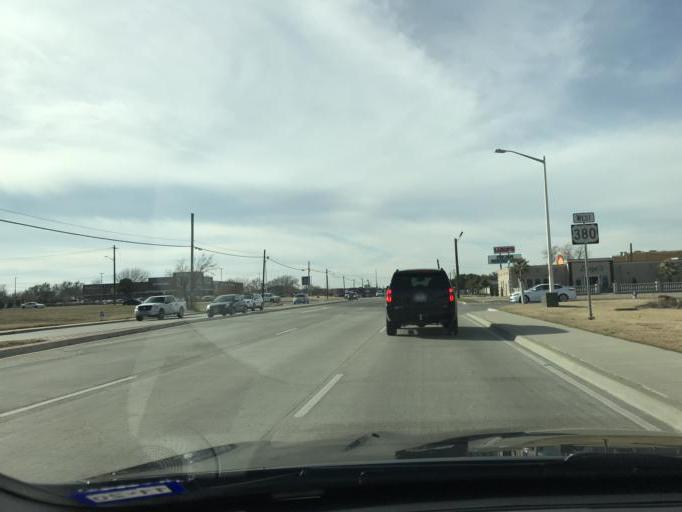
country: US
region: Texas
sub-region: Denton County
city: Denton
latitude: 33.2297
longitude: -97.1537
